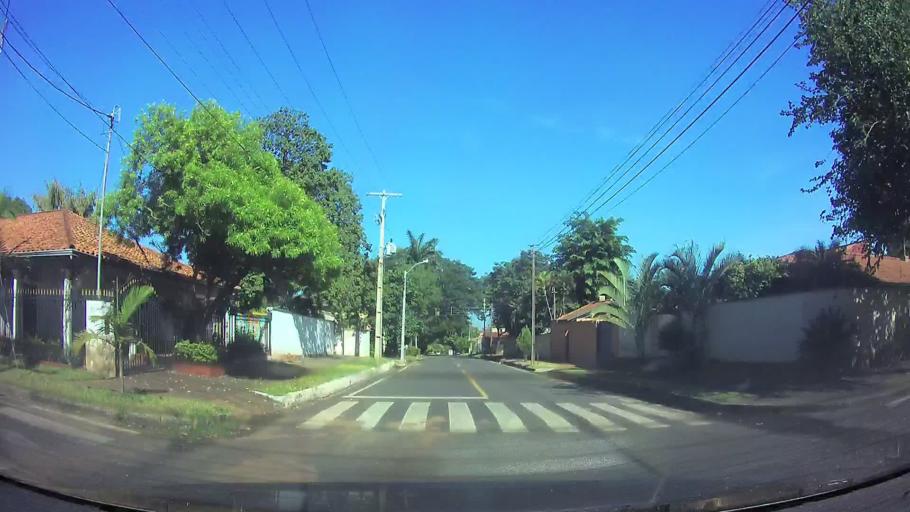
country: PY
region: Central
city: Fernando de la Mora
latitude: -25.2686
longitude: -57.5128
